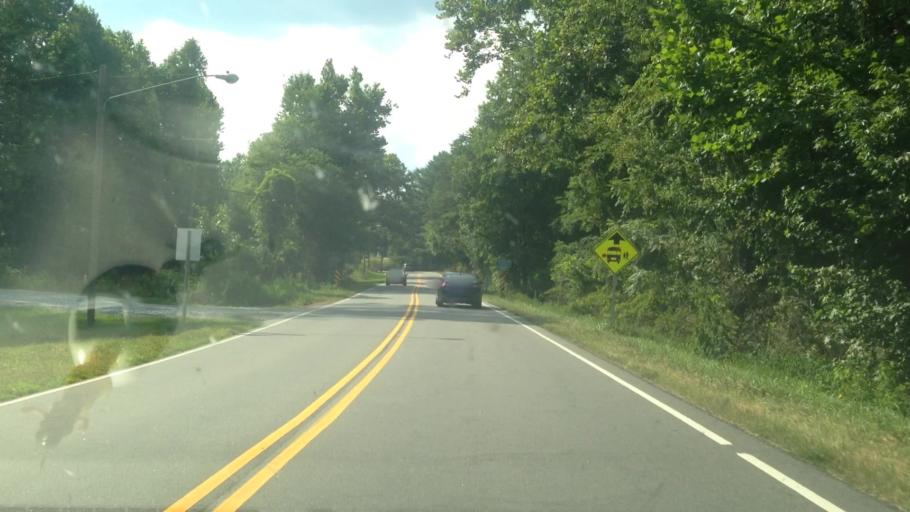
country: US
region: North Carolina
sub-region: Forsyth County
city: Kernersville
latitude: 36.1266
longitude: -80.1129
